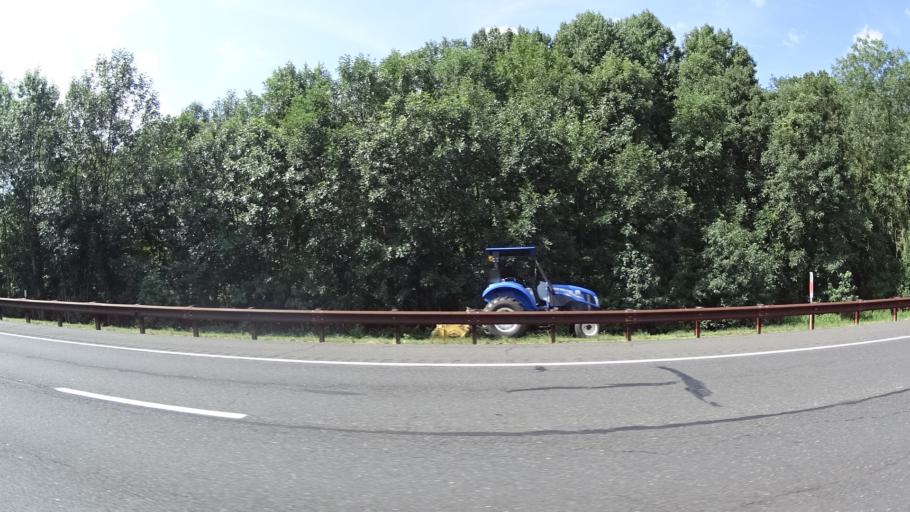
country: US
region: New Jersey
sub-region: Monmouth County
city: Lincroft
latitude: 40.3596
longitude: -74.1350
